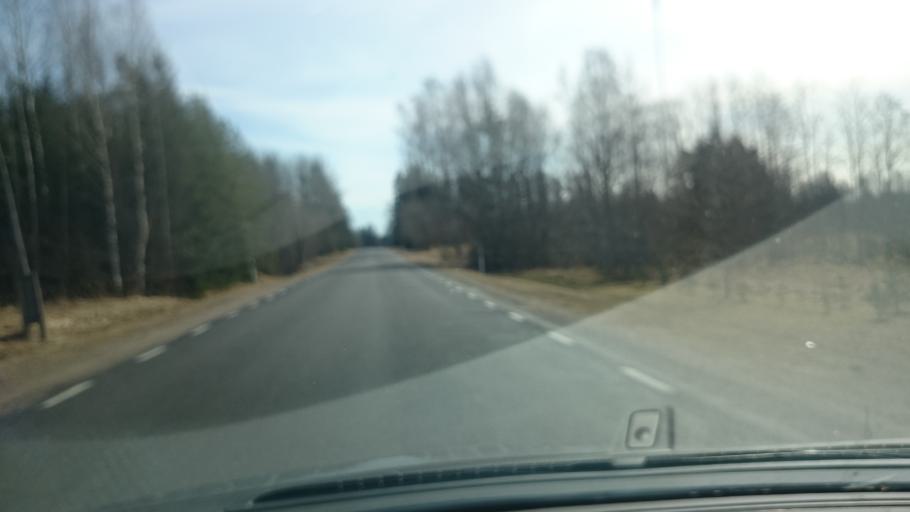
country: EE
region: Paernumaa
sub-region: Vaendra vald (alev)
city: Vandra
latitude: 58.6307
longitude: 24.9184
